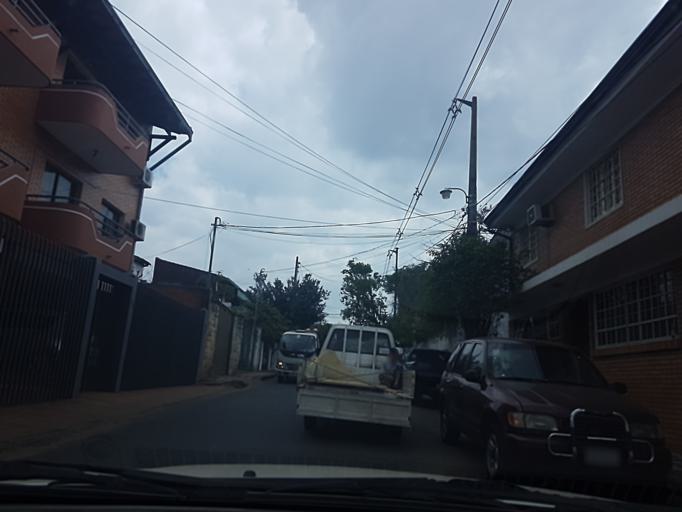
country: PY
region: Asuncion
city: Asuncion
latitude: -25.3092
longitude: -57.6011
